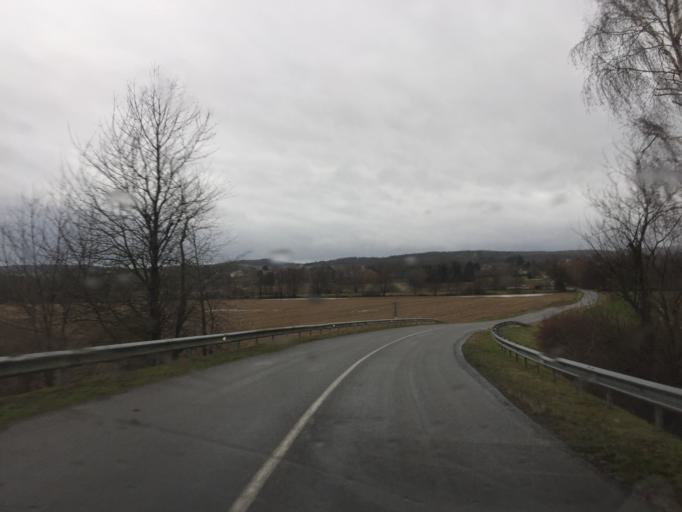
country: FR
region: Franche-Comte
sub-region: Departement du Jura
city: Dole
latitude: 47.1446
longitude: 5.5639
